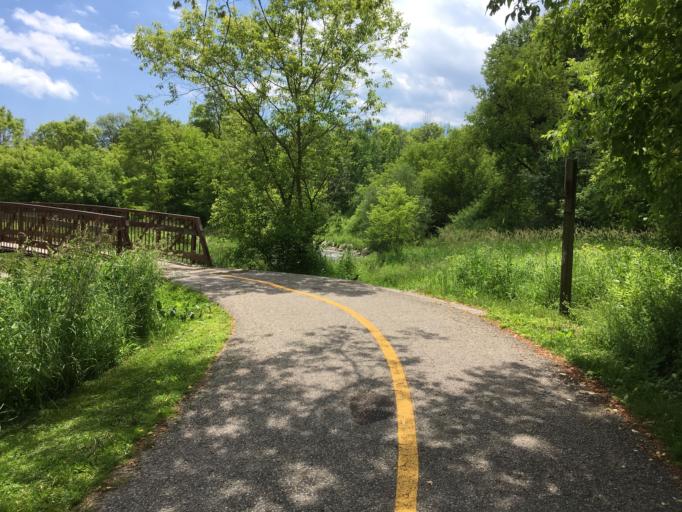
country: CA
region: Ontario
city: Oshawa
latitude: 43.8742
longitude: -78.8531
